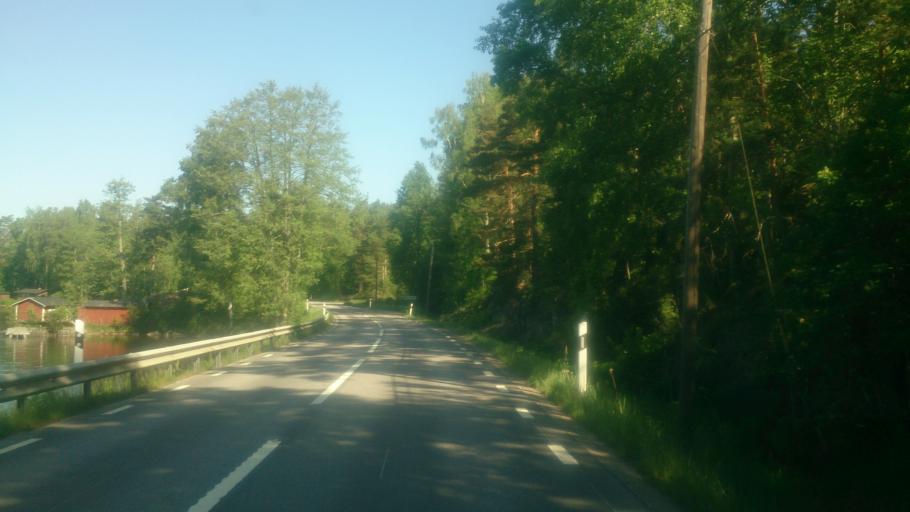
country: SE
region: OEstergoetland
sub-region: Atvidabergs Kommun
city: Atvidaberg
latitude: 58.1014
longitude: 16.1181
